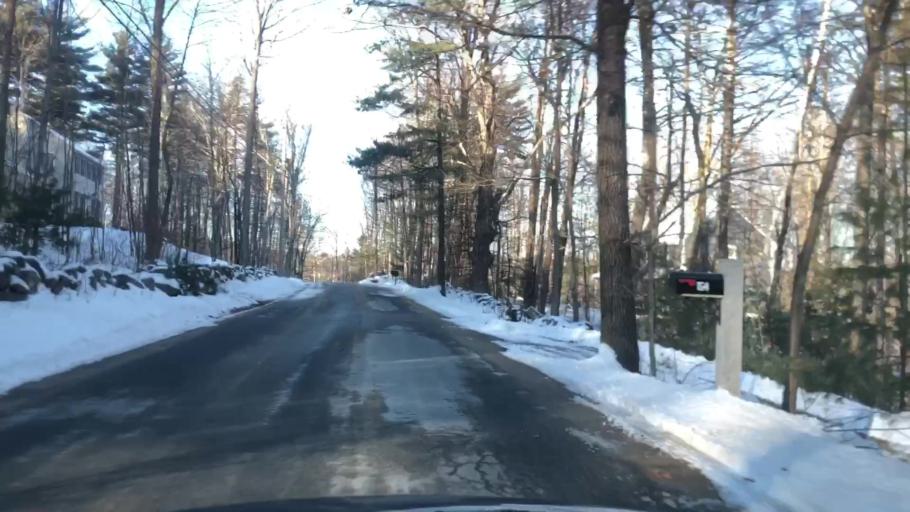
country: US
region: New Hampshire
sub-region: Hillsborough County
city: Wilton
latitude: 42.8030
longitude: -71.7064
